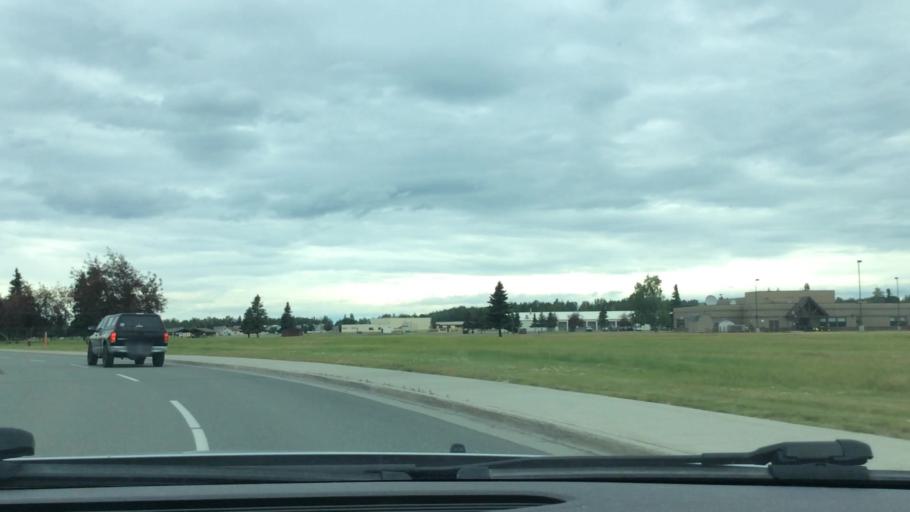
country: US
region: Alaska
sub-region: Anchorage Municipality
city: Anchorage
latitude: 61.2373
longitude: -149.8500
